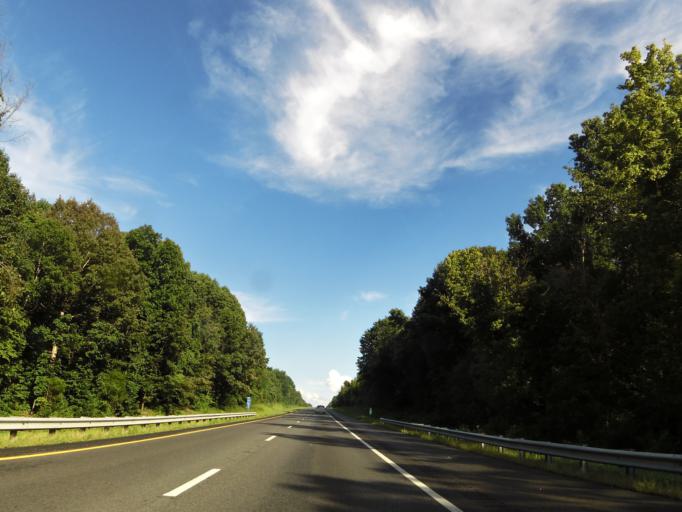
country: US
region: Kentucky
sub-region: Todd County
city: Guthrie
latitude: 36.4949
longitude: -87.1744
